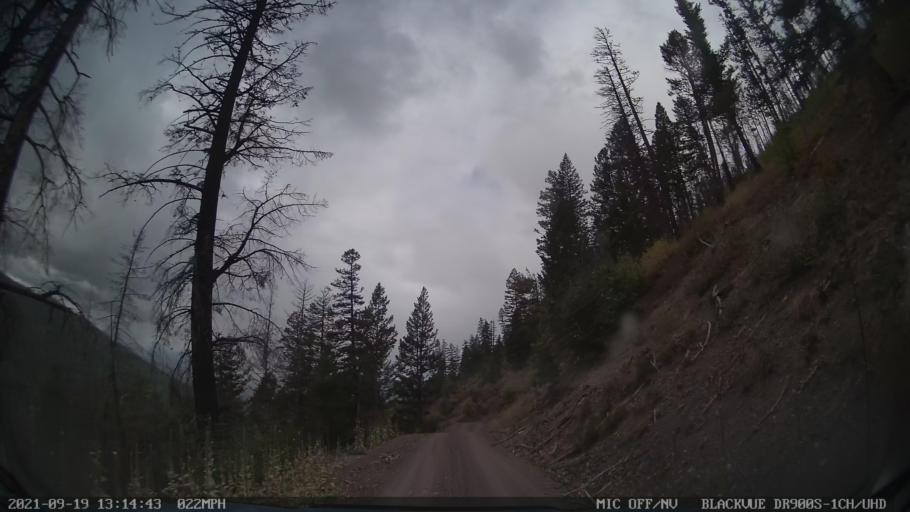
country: US
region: Montana
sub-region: Missoula County
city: Seeley Lake
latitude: 47.1784
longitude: -113.3644
